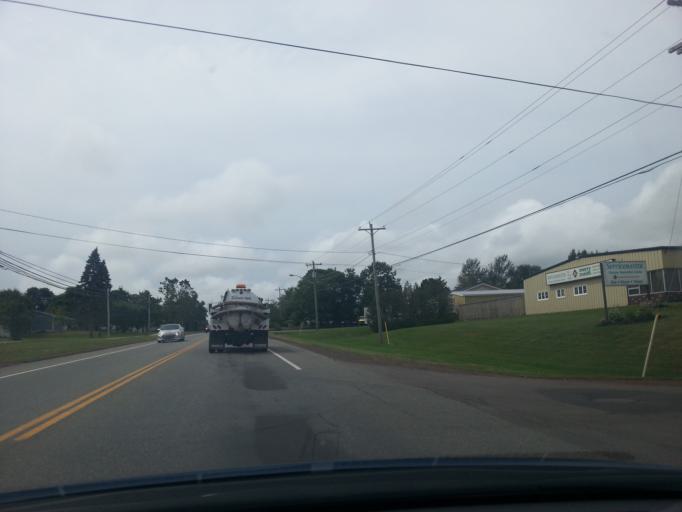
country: CA
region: Prince Edward Island
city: Charlottetown
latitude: 46.2857
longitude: -63.0933
